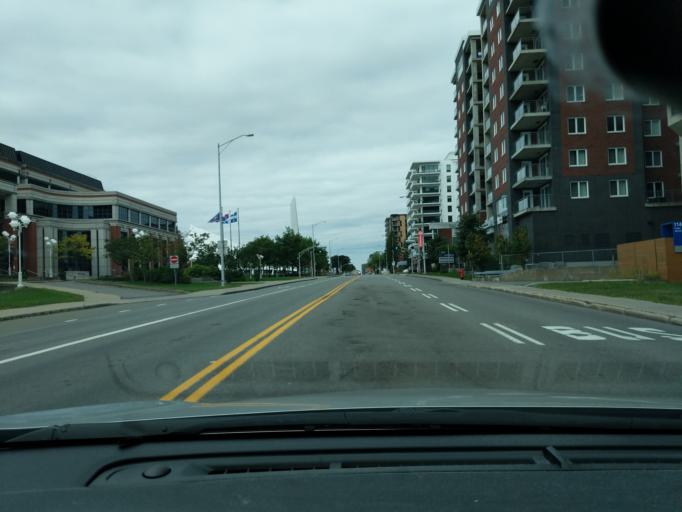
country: CA
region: Quebec
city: L'Ancienne-Lorette
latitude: 46.7690
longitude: -71.2915
